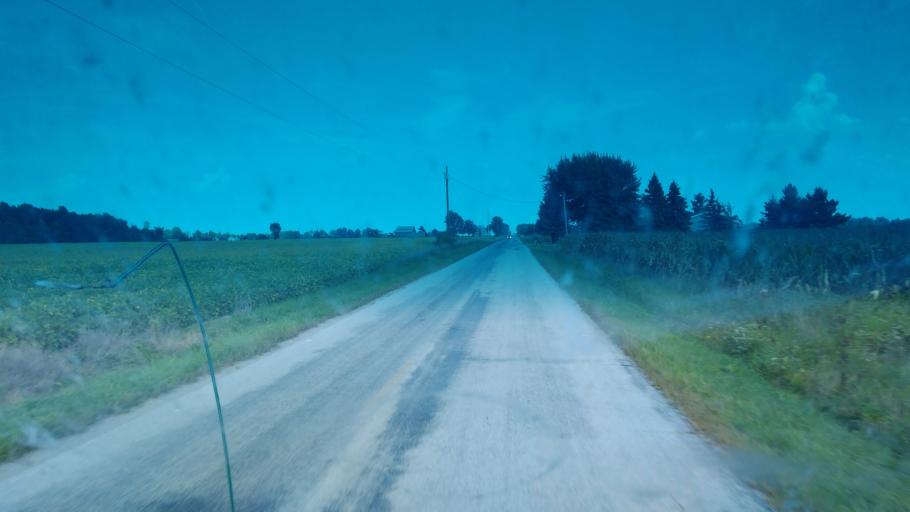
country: US
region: Ohio
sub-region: Wyandot County
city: Carey
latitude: 40.9050
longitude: -83.4768
